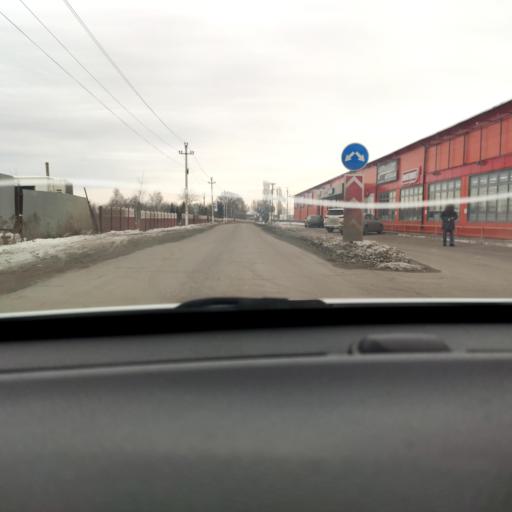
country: RU
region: Voronezj
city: Novaya Usman'
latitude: 51.6695
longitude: 39.3363
